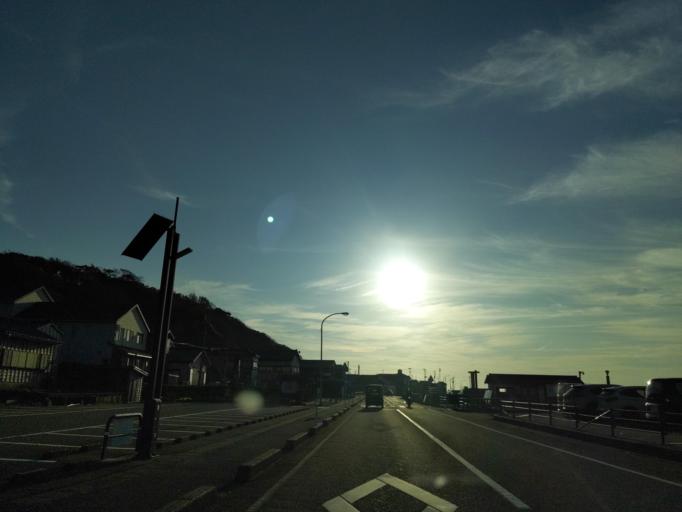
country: JP
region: Niigata
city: Nagaoka
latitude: 37.5454
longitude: 138.6920
